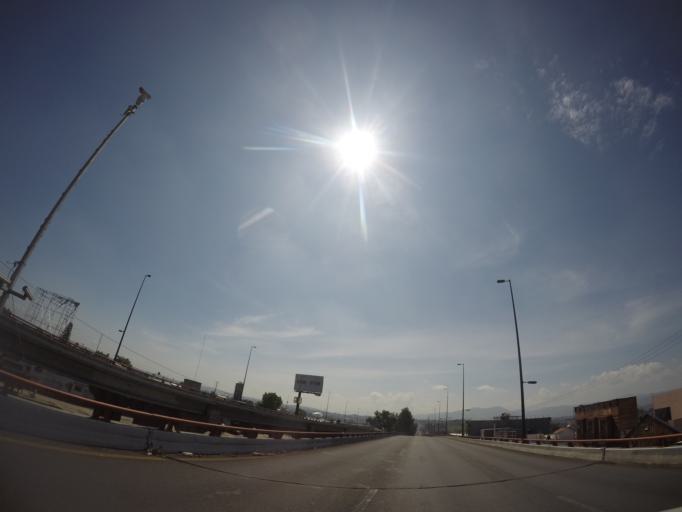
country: MX
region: Michoacan
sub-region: Tarimbaro
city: Real Hacienda (Metropolis)
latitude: 19.7263
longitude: -101.2117
